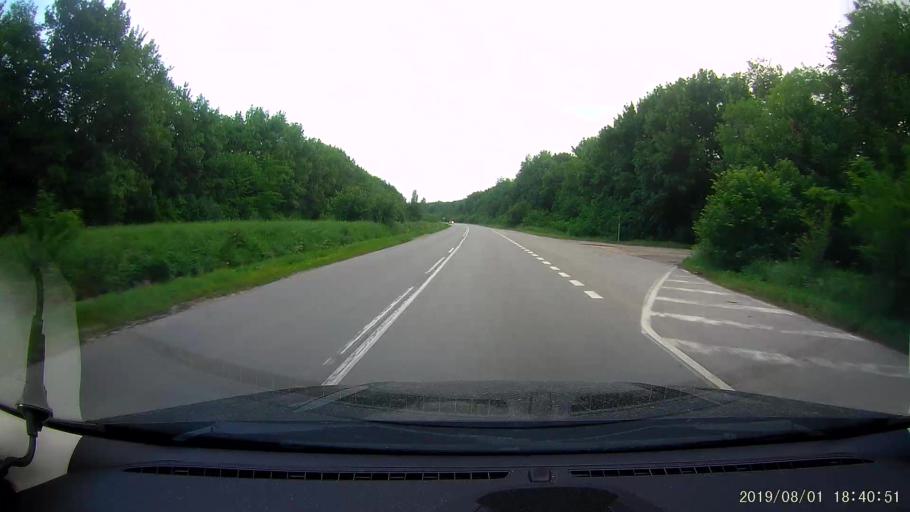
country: BG
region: Shumen
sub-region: Obshtina Khitrino
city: Gara Khitrino
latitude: 43.3574
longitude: 26.9212
